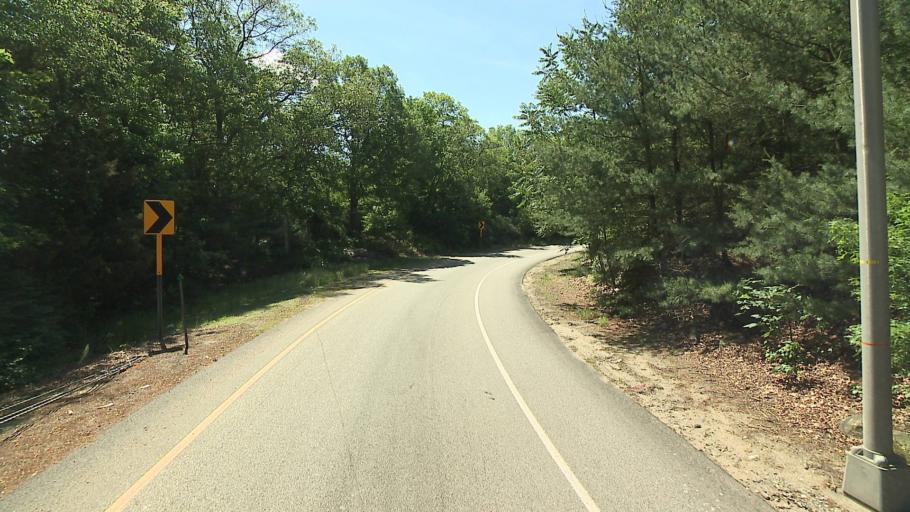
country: US
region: Connecticut
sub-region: New London County
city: Norwich
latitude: 41.5473
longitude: -72.1067
